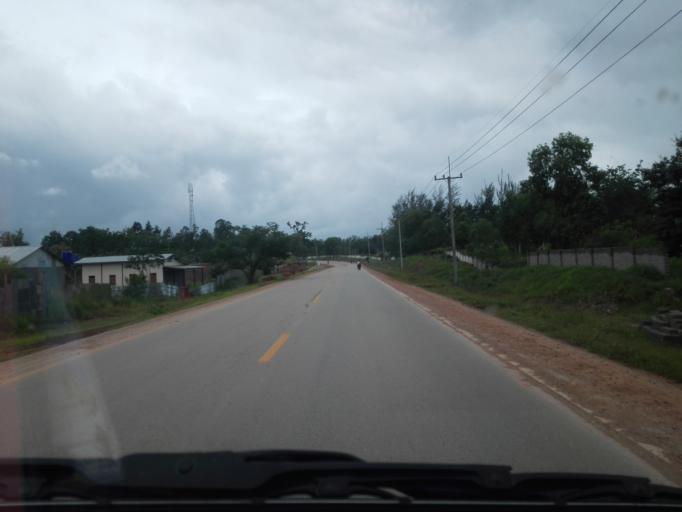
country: TH
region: Tak
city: Mae Sot
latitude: 16.6919
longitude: 98.4519
